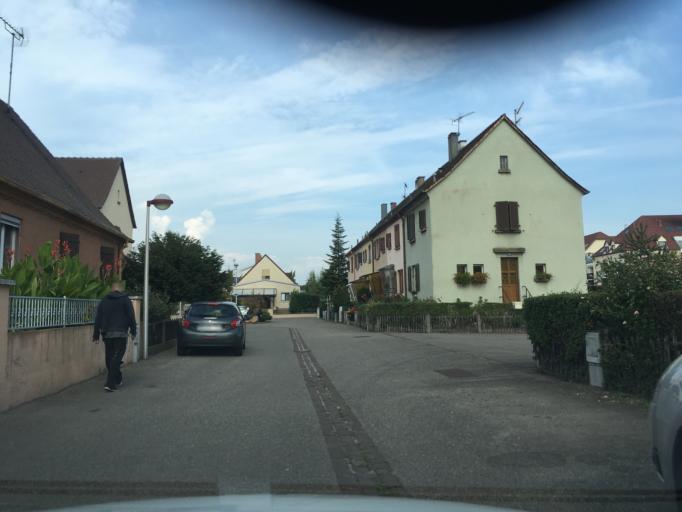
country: FR
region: Alsace
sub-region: Departement du Haut-Rhin
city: Colmar
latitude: 48.0892
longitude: 7.3584
